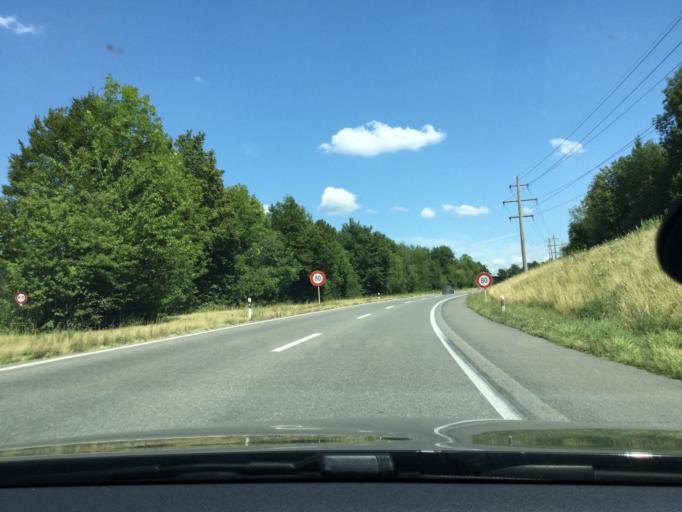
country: CH
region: Vaud
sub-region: Ouest Lausannois District
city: Ecublens
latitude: 46.5404
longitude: 6.5616
